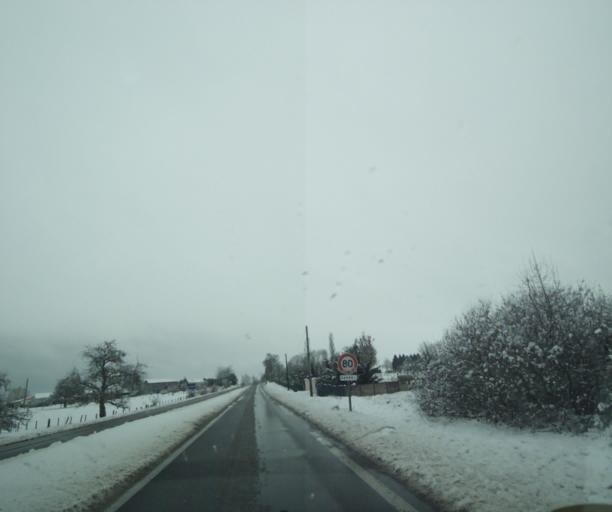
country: FR
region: Champagne-Ardenne
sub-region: Departement de la Haute-Marne
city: Montier-en-Der
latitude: 48.5217
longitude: 4.8110
